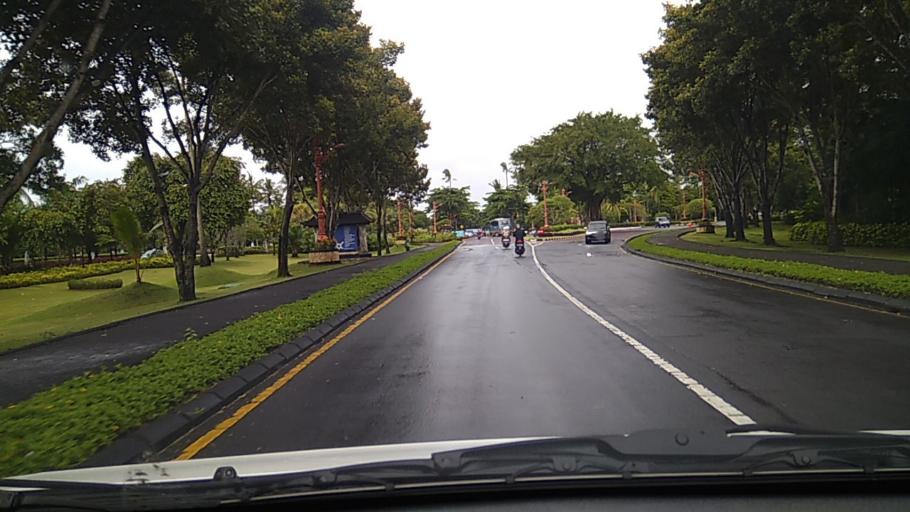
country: ID
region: Bali
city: Bualu
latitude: -8.7982
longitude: 115.2286
